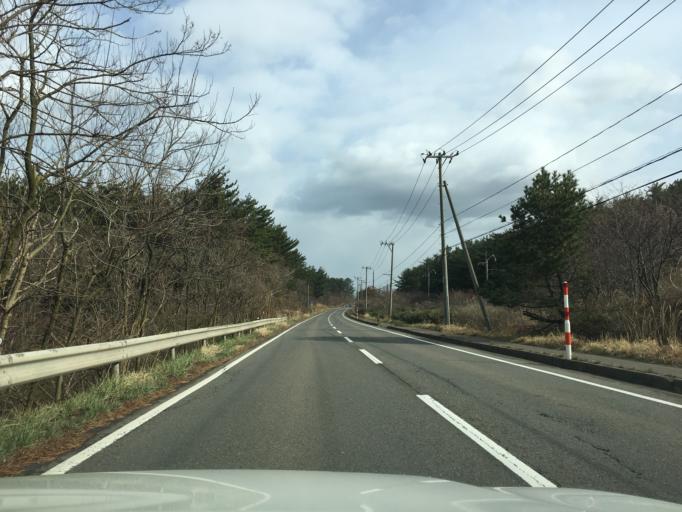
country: JP
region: Yamagata
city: Yuza
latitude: 39.2284
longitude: 139.9061
